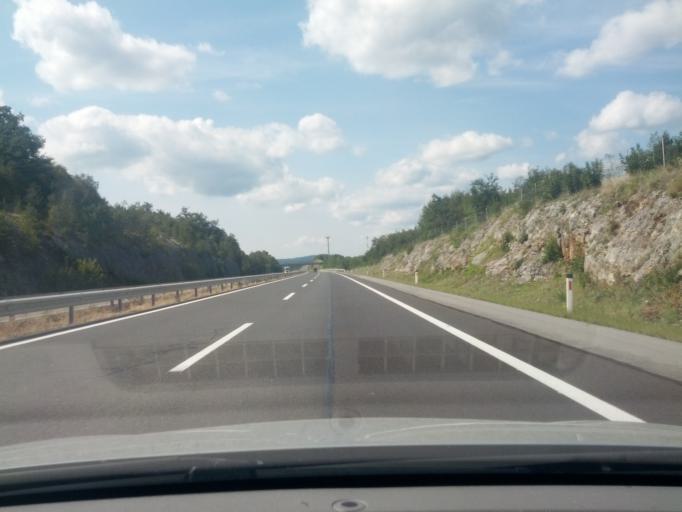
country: SI
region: Divaca
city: Divaca
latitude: 45.7091
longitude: 13.9250
